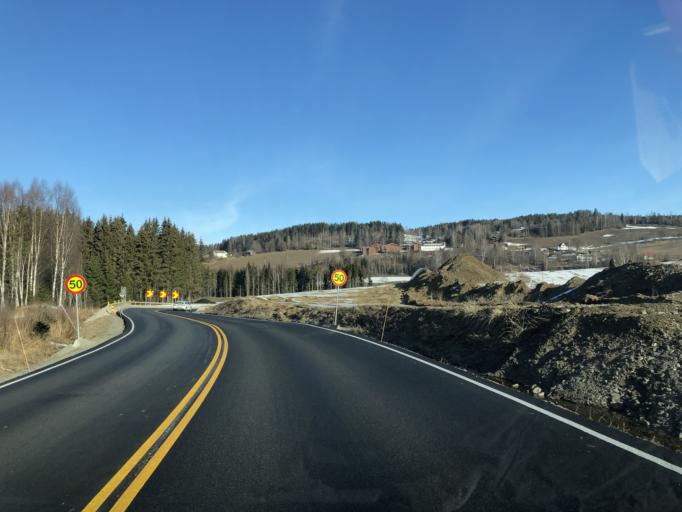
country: NO
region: Hedmark
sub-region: Ringsaker
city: Moelv
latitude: 60.9069
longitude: 10.7360
